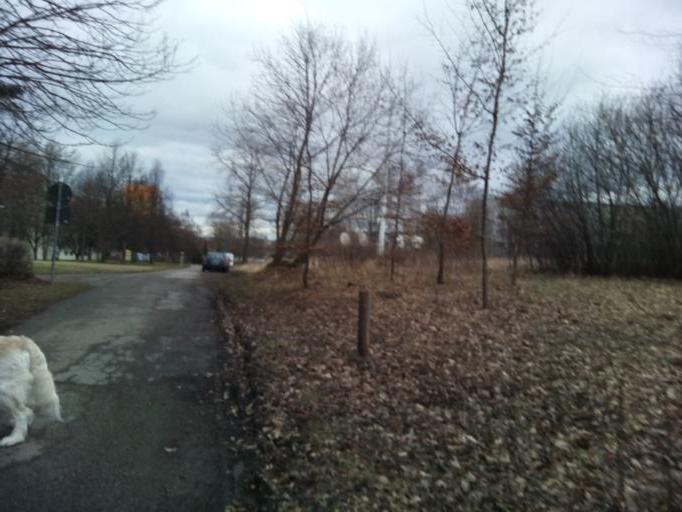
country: DE
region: Saxony
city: Freiberg
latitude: 50.9014
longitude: 13.3252
